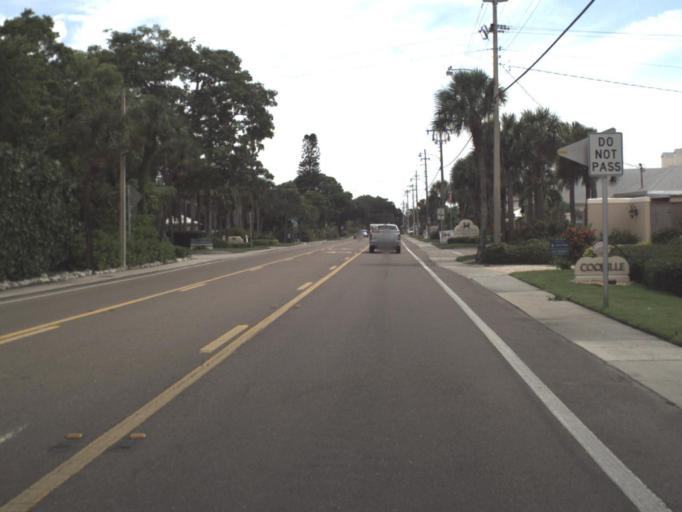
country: US
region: Florida
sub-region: Sarasota County
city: Gulf Gate Estates
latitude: 27.2604
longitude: -82.5396
